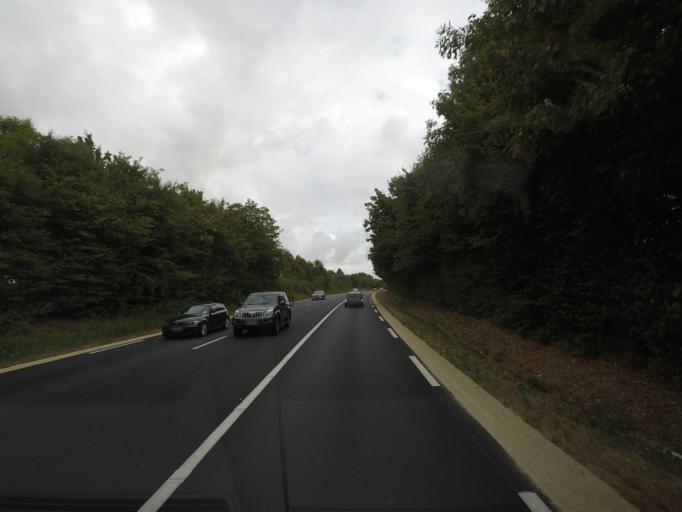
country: FR
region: Poitou-Charentes
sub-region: Departement des Deux-Sevres
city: Celles-sur-Belle
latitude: 46.2637
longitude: -0.2276
